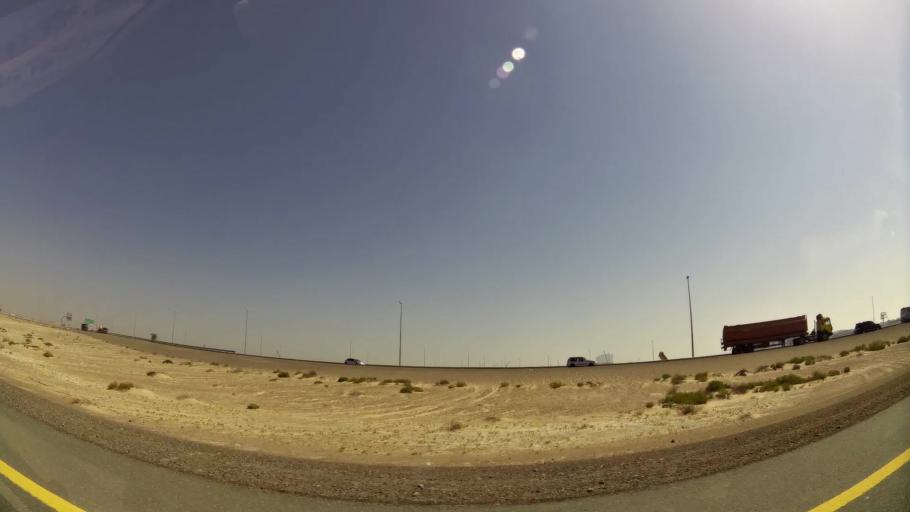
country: AE
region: Dubai
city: Dubai
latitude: 24.9433
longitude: 55.0656
